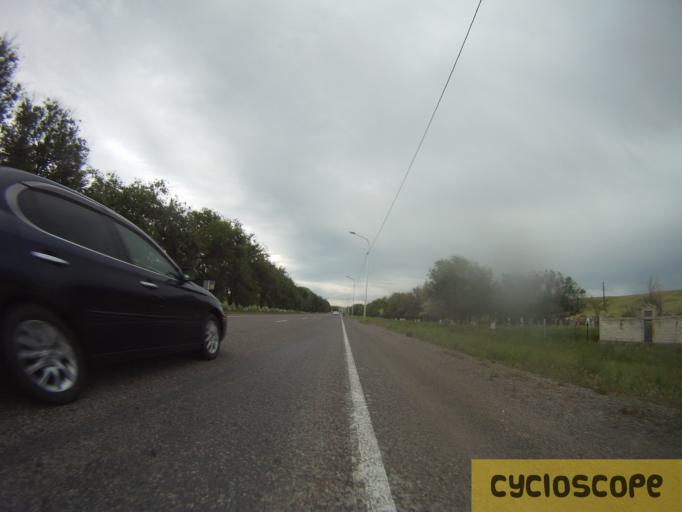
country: KZ
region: Zhambyl
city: Georgiyevka
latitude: 43.2378
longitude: 74.7638
